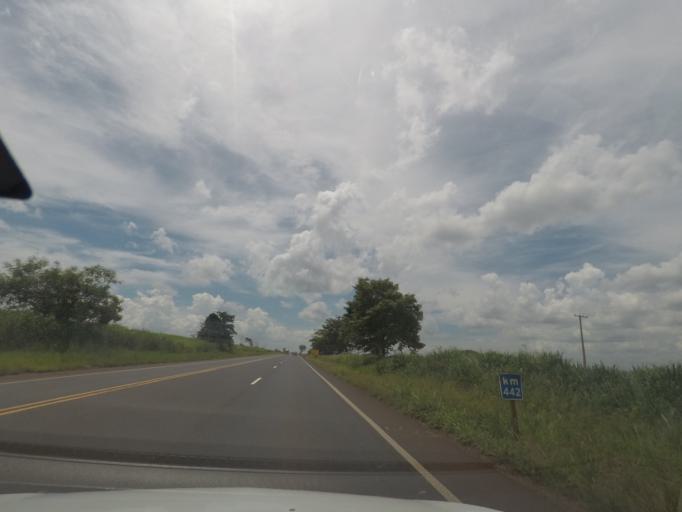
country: BR
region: Sao Paulo
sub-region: Barretos
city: Barretos
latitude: -20.3946
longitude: -48.6385
